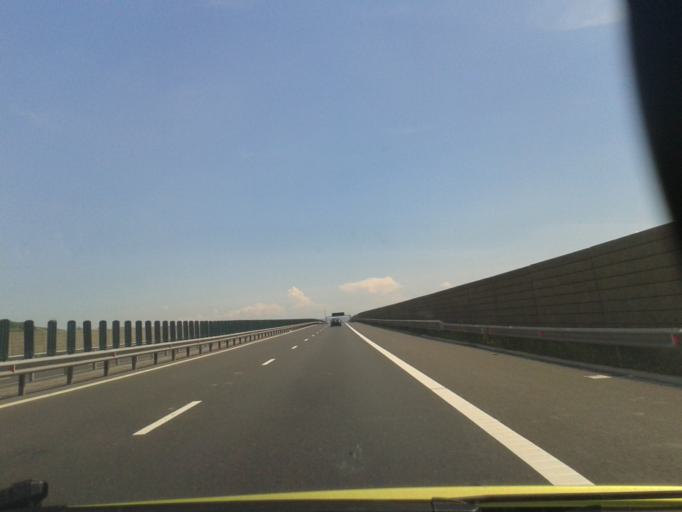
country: RO
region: Alba
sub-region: Comuna Garbova
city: Garbova
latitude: 45.9103
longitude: 23.7398
